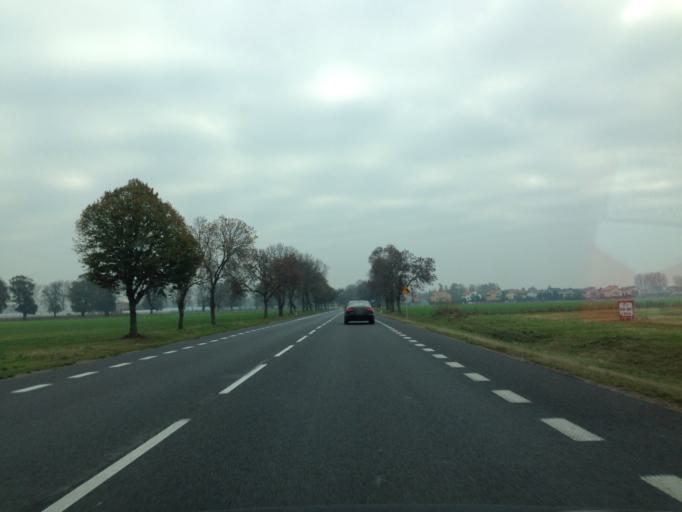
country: PL
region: Masovian Voivodeship
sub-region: Powiat plocki
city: Drobin
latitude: 52.7471
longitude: 19.9768
